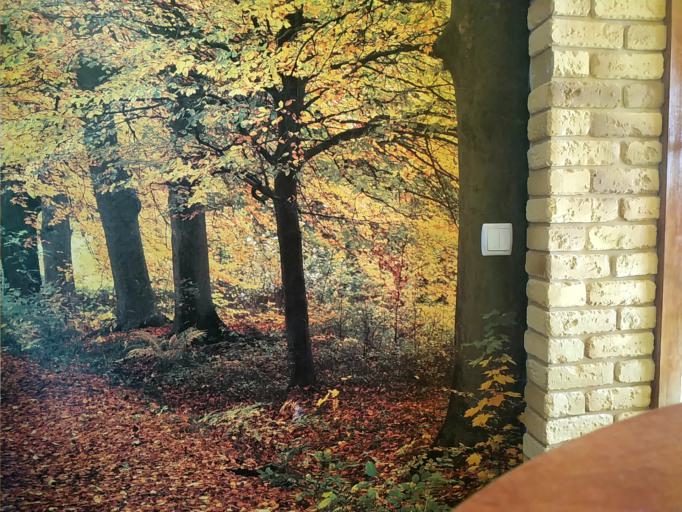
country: RU
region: Jaroslavl
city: Kukoboy
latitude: 58.8743
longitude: 39.7169
